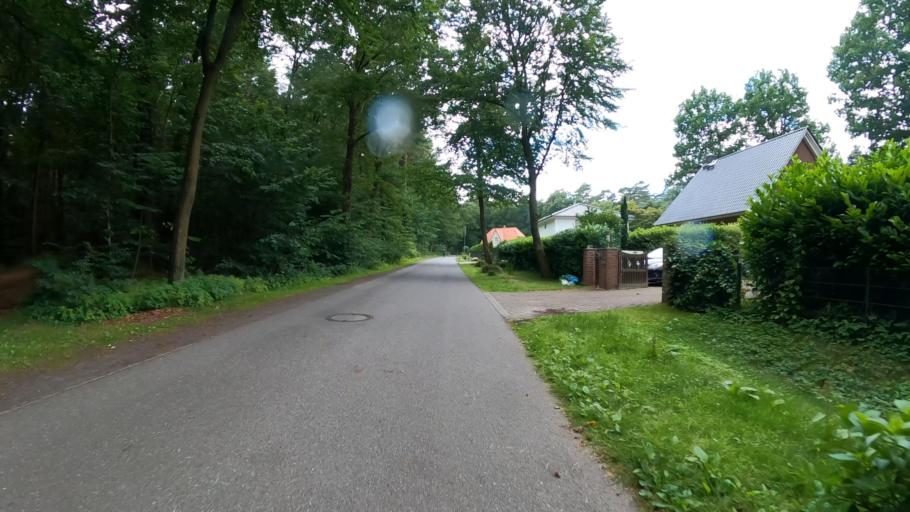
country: DE
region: Lower Saxony
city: Seevetal
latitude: 53.4172
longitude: 9.8820
